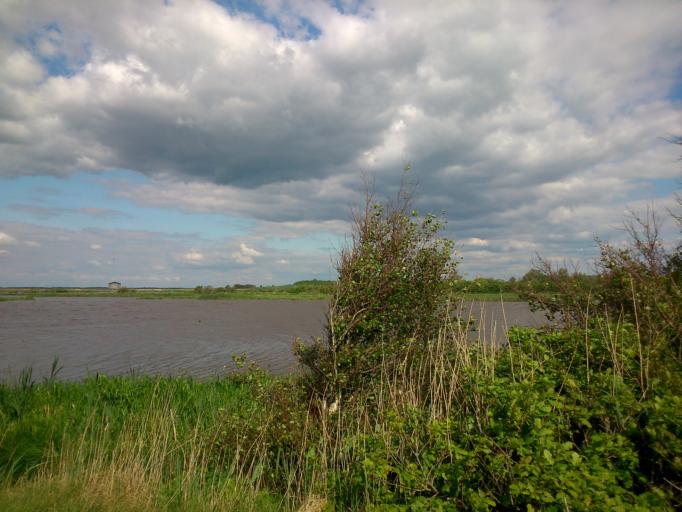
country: DK
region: Central Jutland
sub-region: Ringkobing-Skjern Kommune
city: Skjern
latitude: 55.9036
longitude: 8.4194
